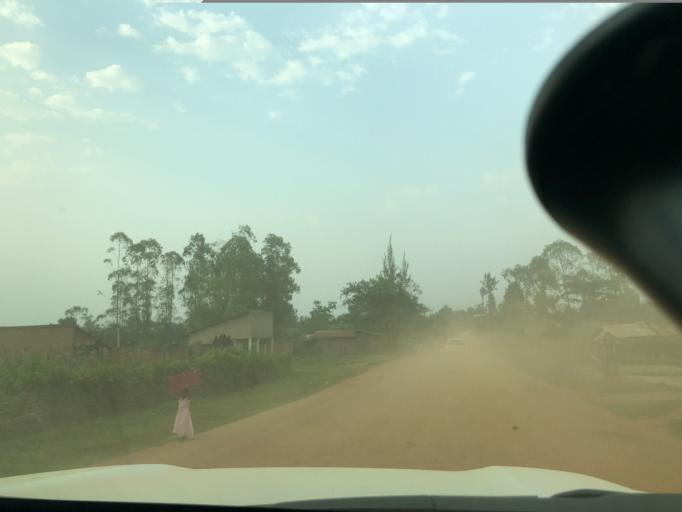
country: UG
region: Western Region
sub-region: Kasese District
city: Margherita
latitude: 0.3231
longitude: 29.6768
